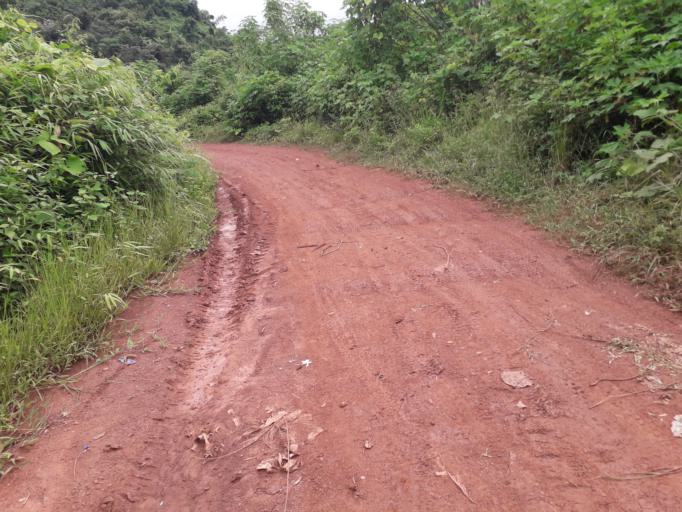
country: CN
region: Yunnan
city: Menglie
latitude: 22.2002
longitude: 101.6784
